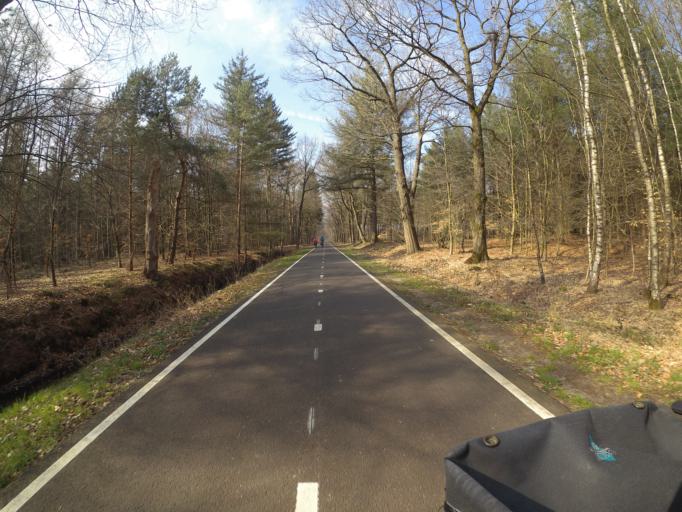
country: NL
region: North Brabant
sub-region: Gemeente Baarle-Nassau
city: Baarle-Nassau
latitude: 51.5138
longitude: 4.8938
